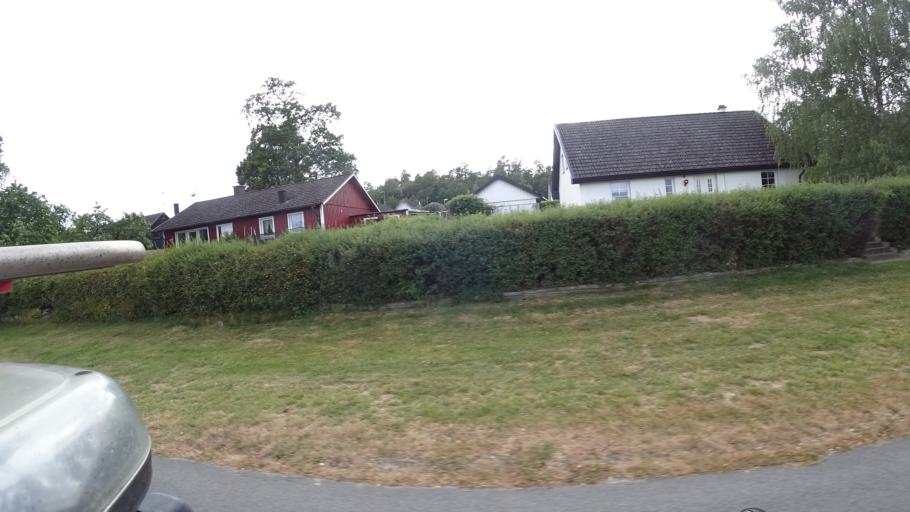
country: SE
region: Skane
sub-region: Ostra Goinge Kommun
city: Knislinge
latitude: 56.1897
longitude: 14.0700
